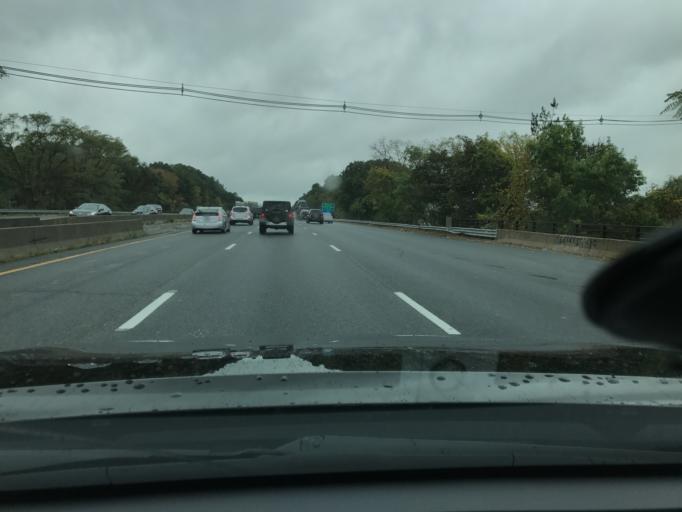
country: US
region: Massachusetts
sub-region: Essex County
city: Lynnfield
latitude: 42.5139
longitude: -71.0284
